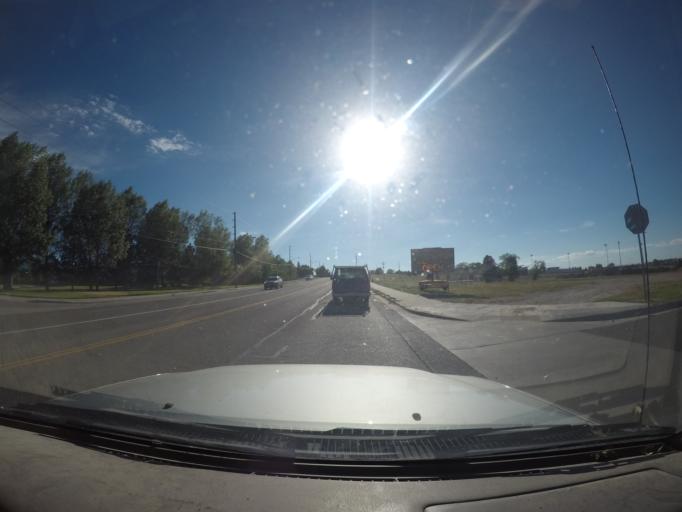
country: US
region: Wyoming
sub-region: Laramie County
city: Fox Farm-College
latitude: 41.1457
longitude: -104.7717
